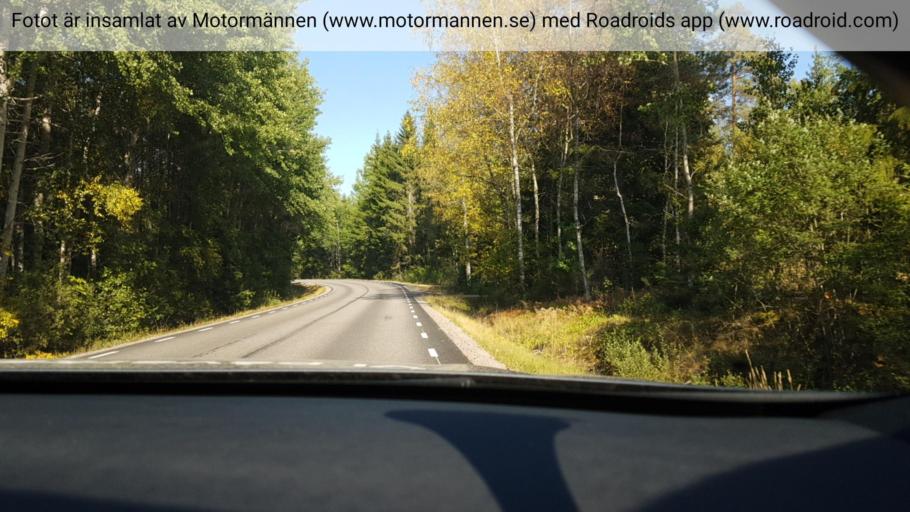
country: SE
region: Vaestra Goetaland
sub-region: Gotene Kommun
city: Goetene
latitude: 58.6314
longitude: 13.5197
